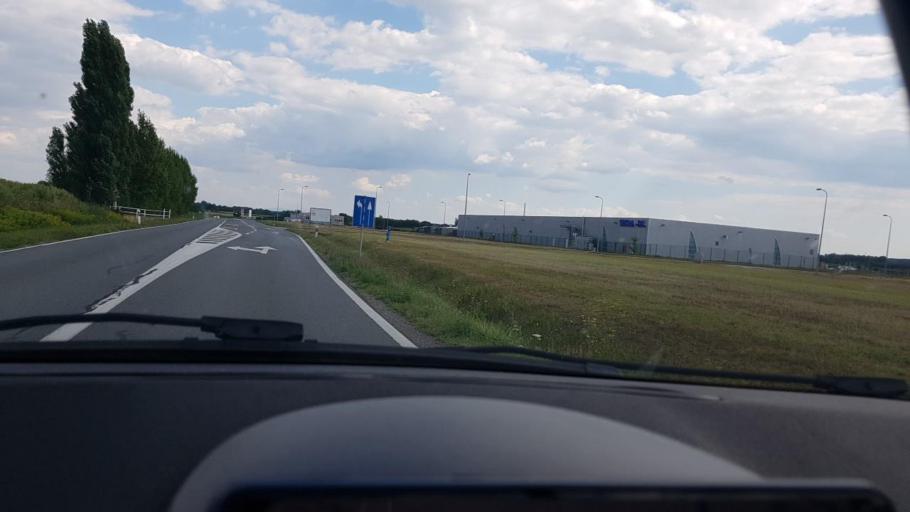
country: HR
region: Bjelovarsko-Bilogorska
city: Zdralovi
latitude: 45.8456
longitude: 16.9460
